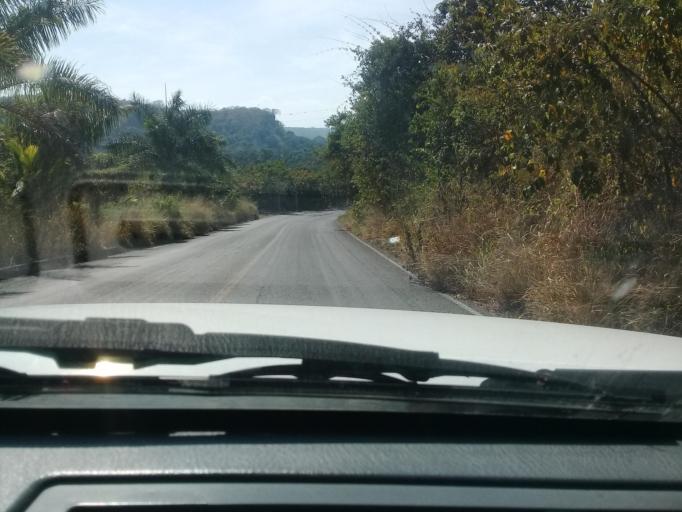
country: MX
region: Veracruz
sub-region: Emiliano Zapata
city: Plan del Rio
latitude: 19.4261
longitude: -96.6080
